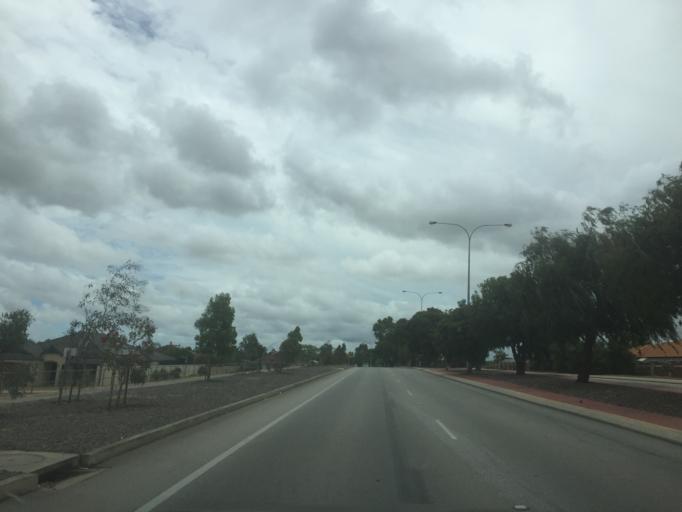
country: AU
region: Western Australia
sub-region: Gosnells
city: Thornlie
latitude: -32.0811
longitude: 115.9500
